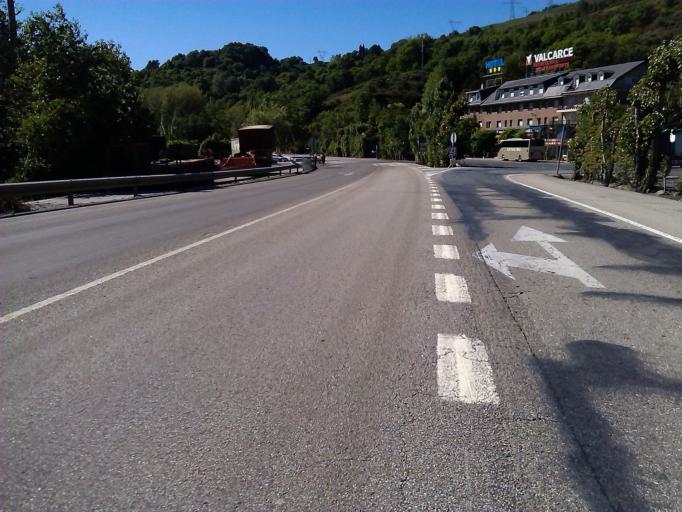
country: ES
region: Castille and Leon
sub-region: Provincia de Leon
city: Vega de Valcarce
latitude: 42.6585
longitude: -6.9144
